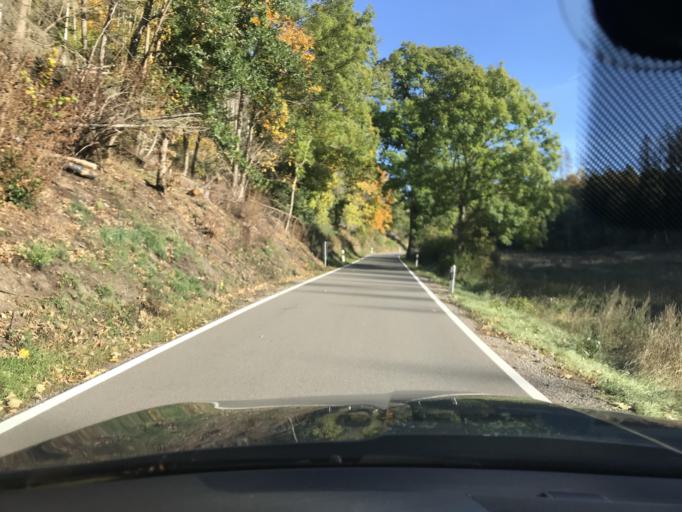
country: DE
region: Saxony-Anhalt
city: Friedrichsbrunn
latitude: 51.6873
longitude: 10.9680
